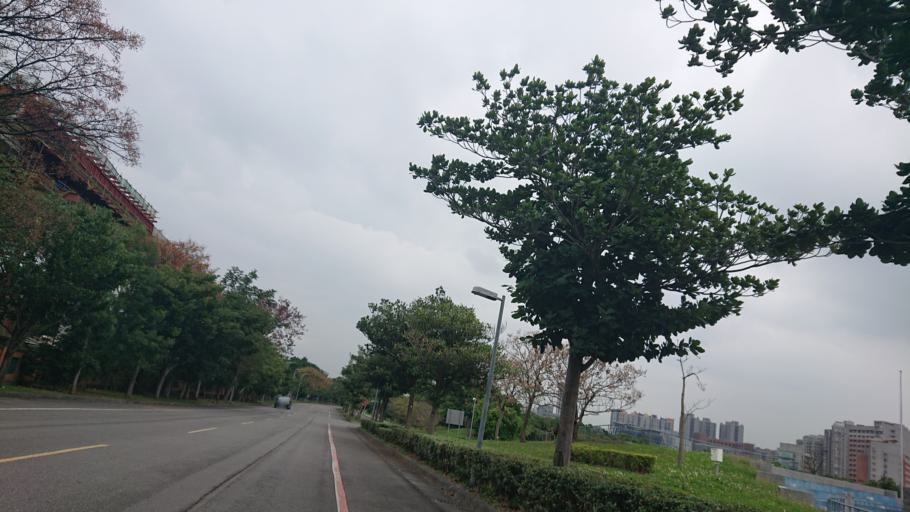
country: TW
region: Taiwan
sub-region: Taoyuan
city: Taoyuan
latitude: 24.9409
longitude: 121.3631
